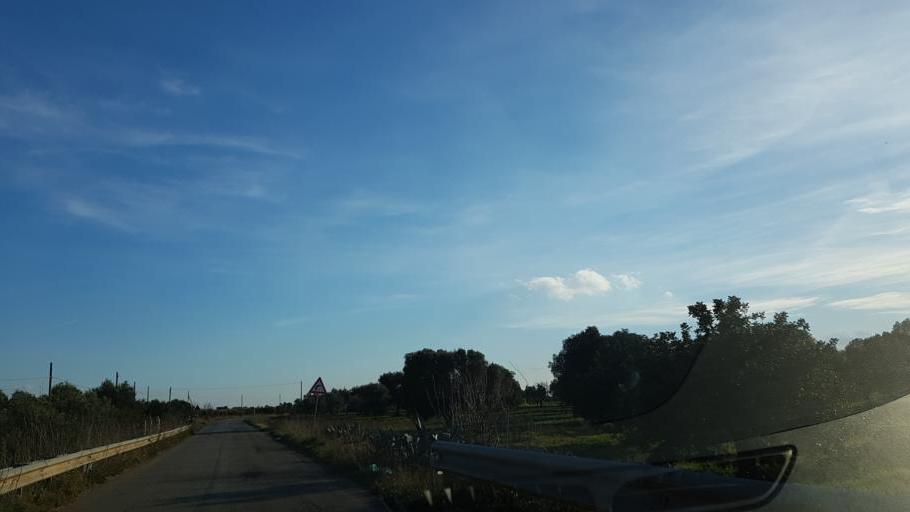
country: IT
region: Apulia
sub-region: Provincia di Brindisi
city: San Vito dei Normanni
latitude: 40.6685
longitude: 17.7796
